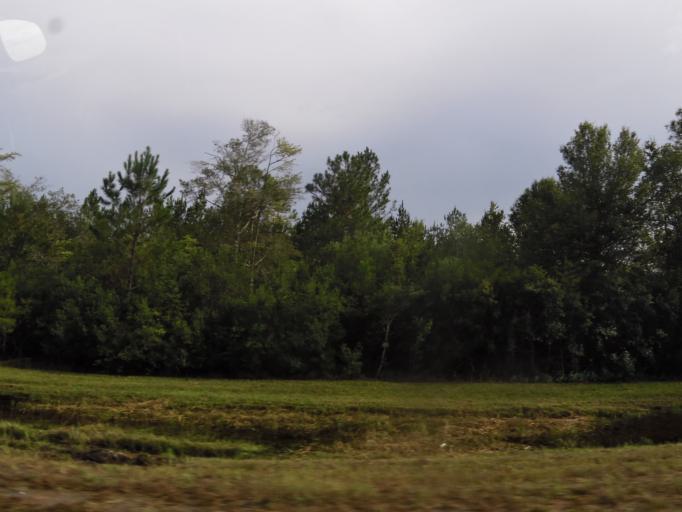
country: US
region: Georgia
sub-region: Liberty County
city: Walthourville
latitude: 31.7470
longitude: -81.6824
